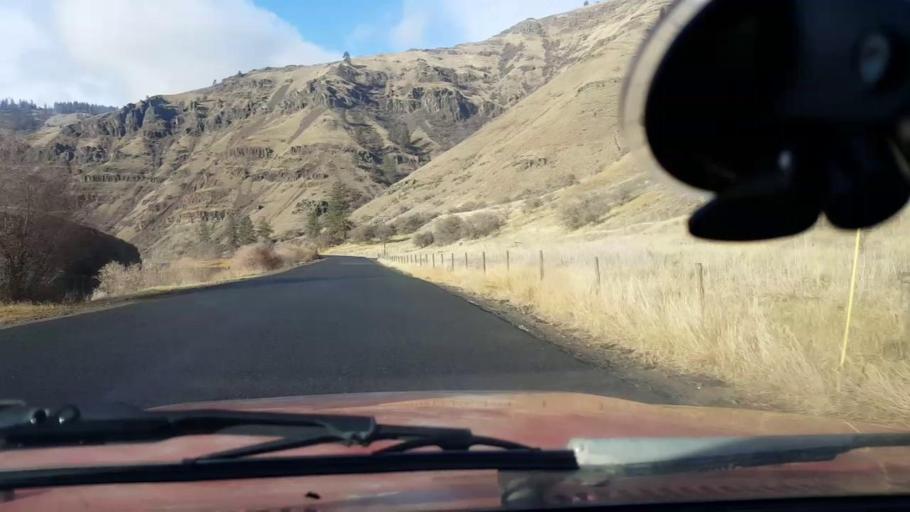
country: US
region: Washington
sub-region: Asotin County
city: Asotin
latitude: 46.0188
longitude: -117.3535
